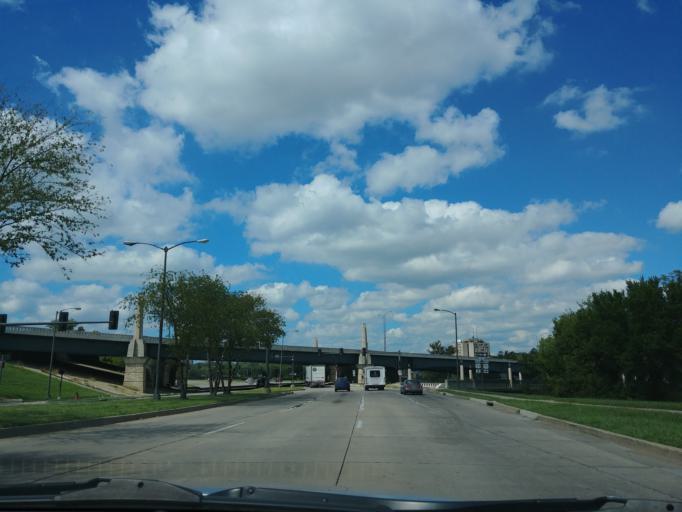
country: US
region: Kansas
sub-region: Johnson County
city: Westwood
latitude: 39.0403
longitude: -94.5575
